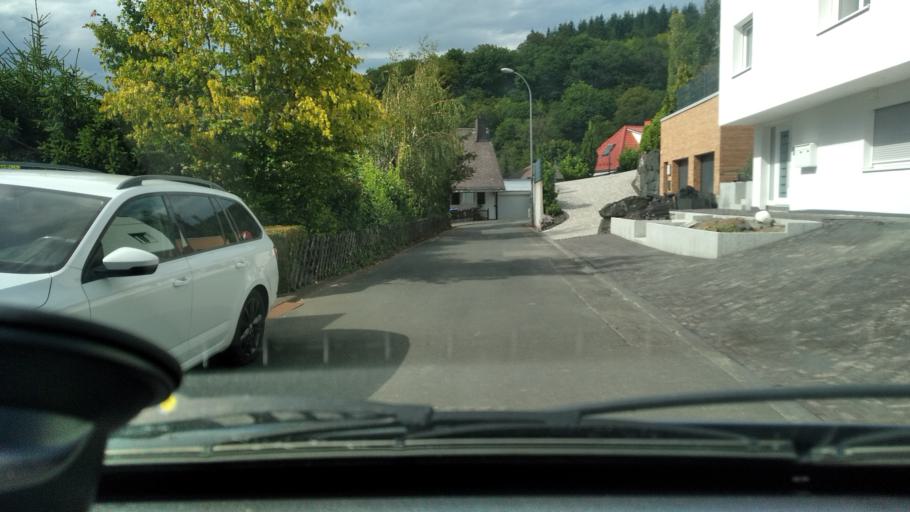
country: DE
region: Hesse
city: Dillenburg
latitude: 50.7375
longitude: 8.2960
